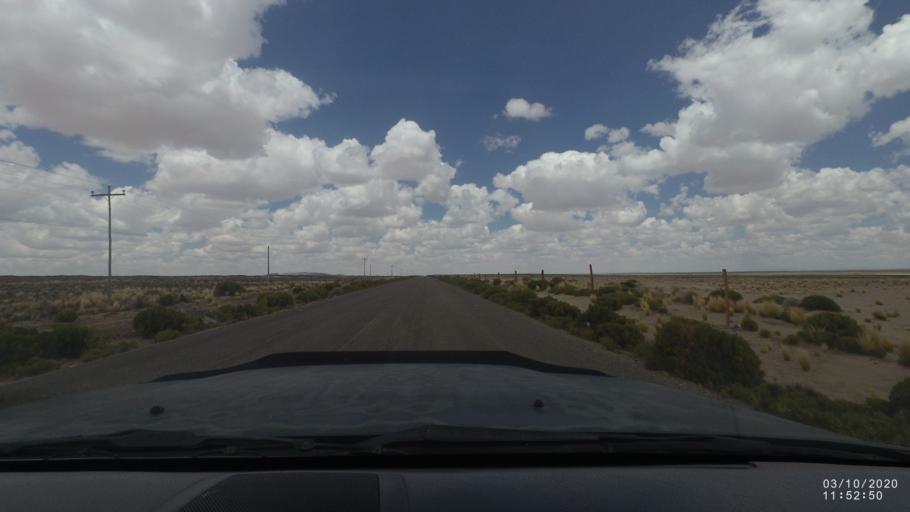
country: BO
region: Oruro
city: Poopo
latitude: -18.4675
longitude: -67.6015
